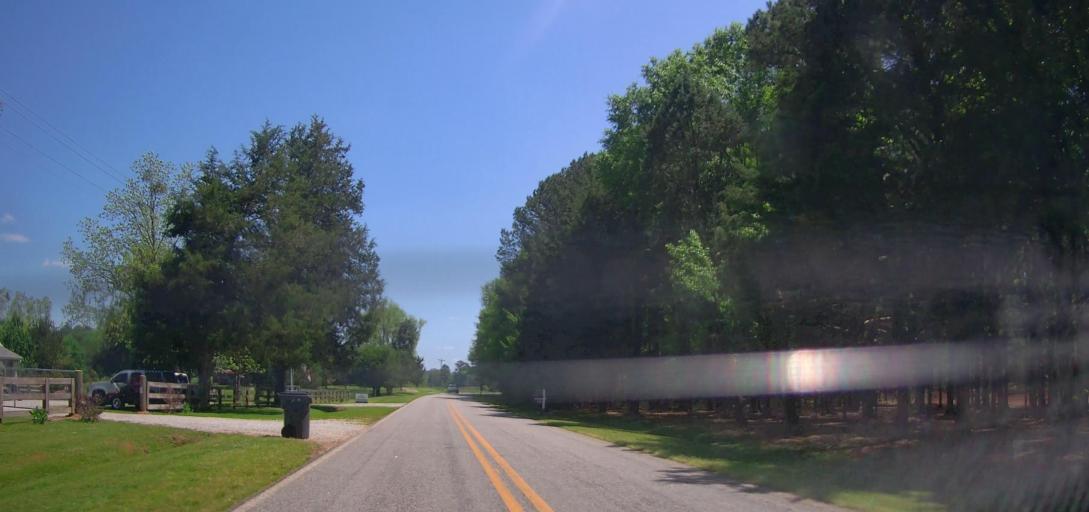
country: US
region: Georgia
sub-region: Jasper County
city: Monticello
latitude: 33.2802
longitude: -83.6712
